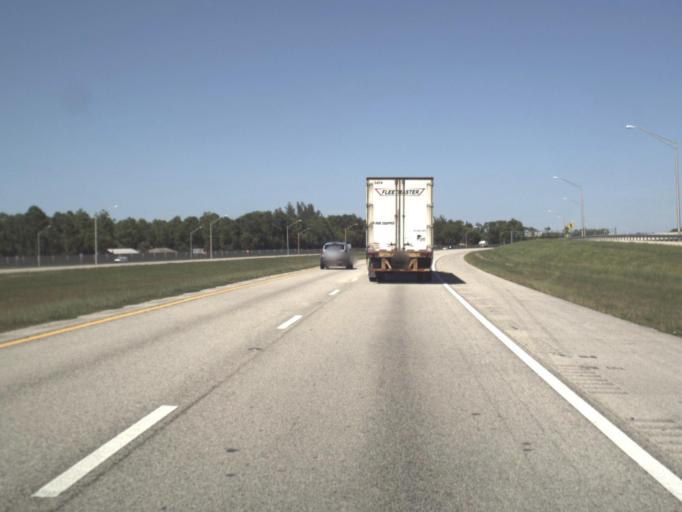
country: US
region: Florida
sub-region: Collier County
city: Golden Gate
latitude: 26.1746
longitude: -81.7343
